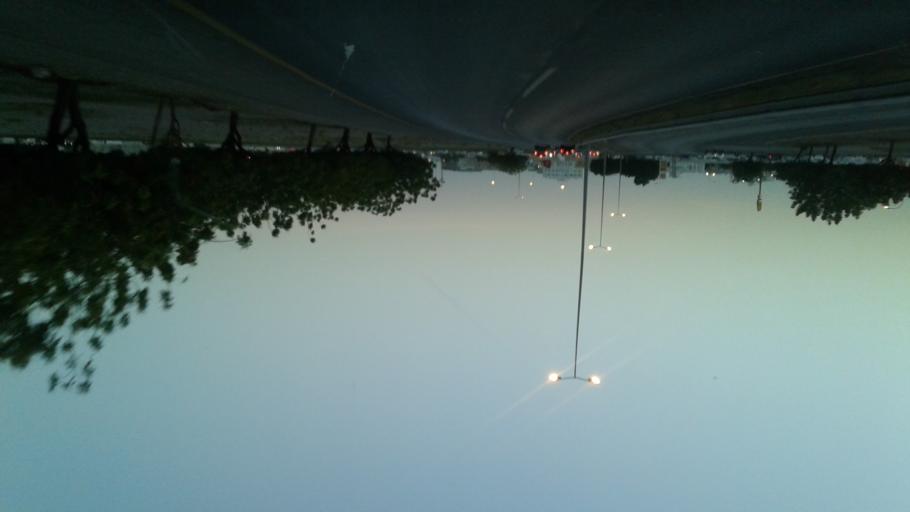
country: OM
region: Muhafazat Masqat
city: As Sib al Jadidah
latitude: 23.6118
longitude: 58.2155
